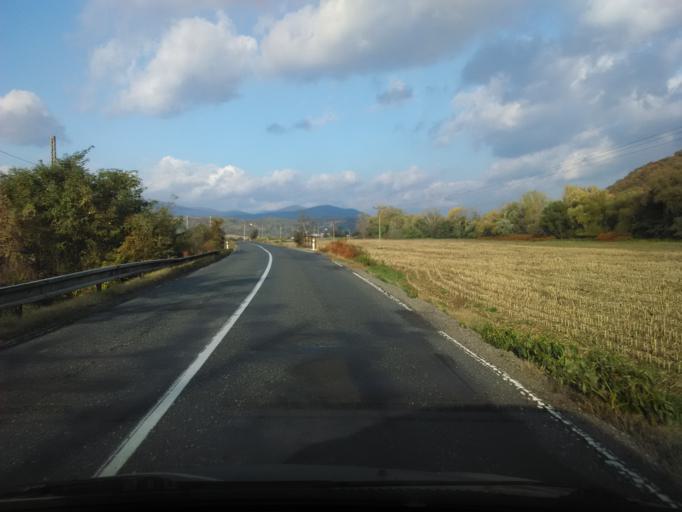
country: SK
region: Nitriansky
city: Tlmace
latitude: 48.3175
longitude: 18.5397
